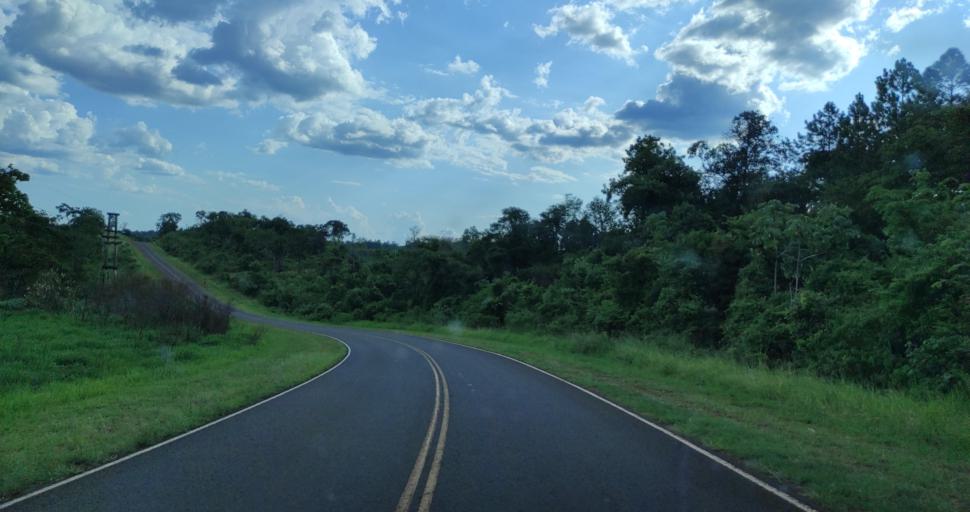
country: AR
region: Misiones
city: San Vicente
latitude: -26.3408
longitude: -54.1810
